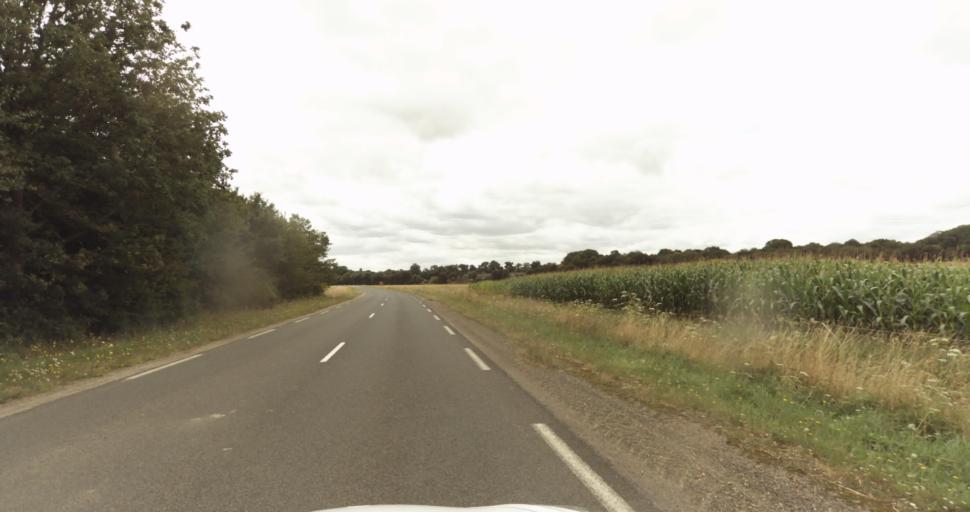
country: FR
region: Haute-Normandie
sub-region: Departement de l'Eure
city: La Madeleine-de-Nonancourt
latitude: 48.8479
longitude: 1.2411
